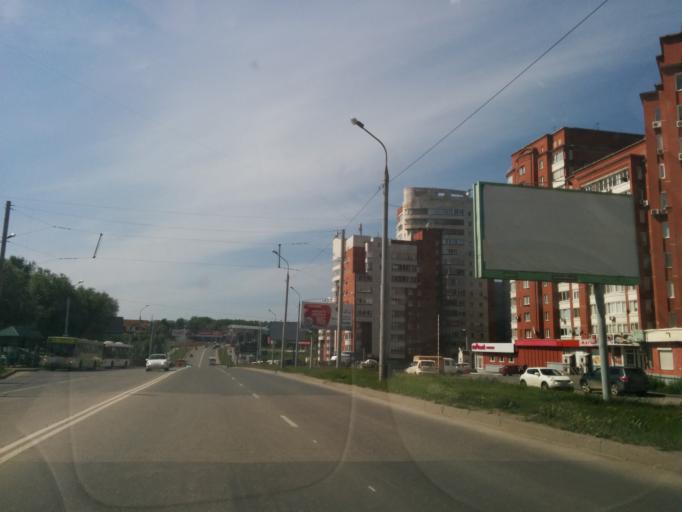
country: RU
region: Perm
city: Perm
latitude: 58.0070
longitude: 56.3026
